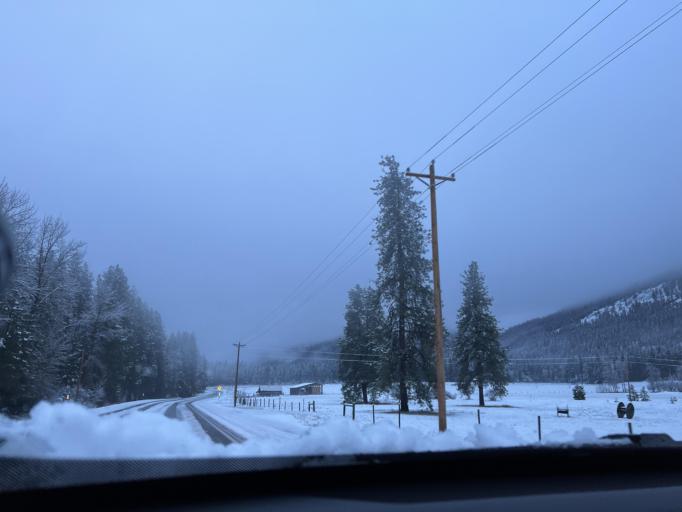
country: US
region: Washington
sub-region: Chelan County
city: Granite Falls
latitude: 48.5747
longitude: -120.3871
